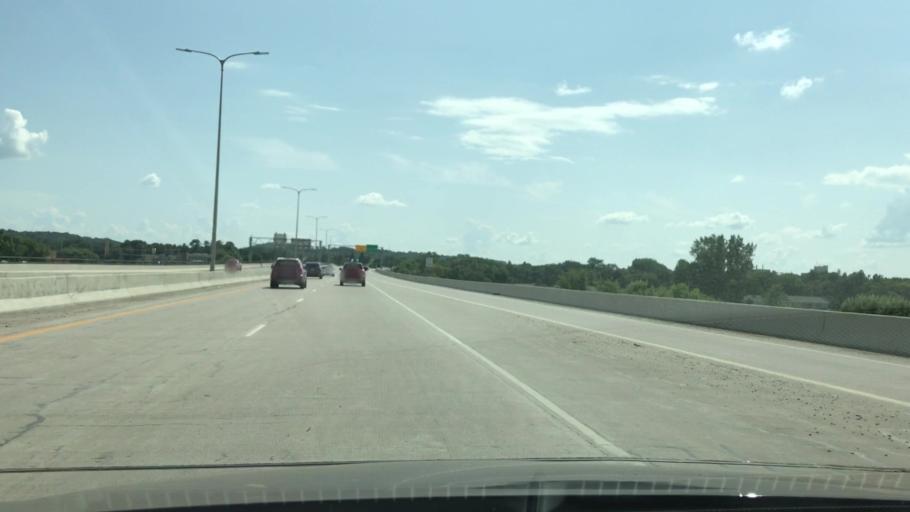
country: US
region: Minnesota
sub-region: Blue Earth County
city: Mankato
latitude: 44.1658
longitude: -94.0170
